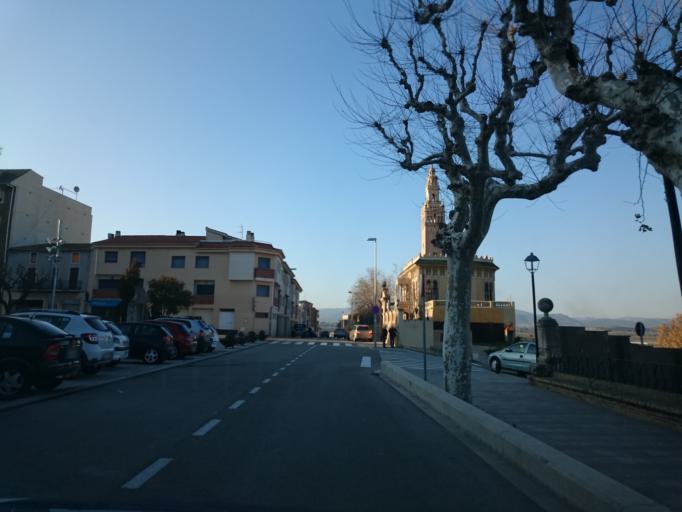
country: ES
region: Catalonia
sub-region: Provincia de Barcelona
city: Castellet
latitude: 41.2685
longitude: 1.6048
